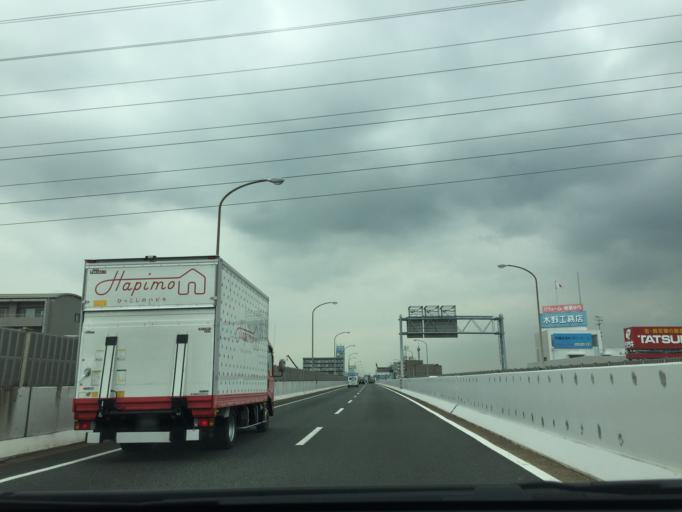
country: JP
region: Aichi
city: Nagoya-shi
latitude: 35.0920
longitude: 136.9305
